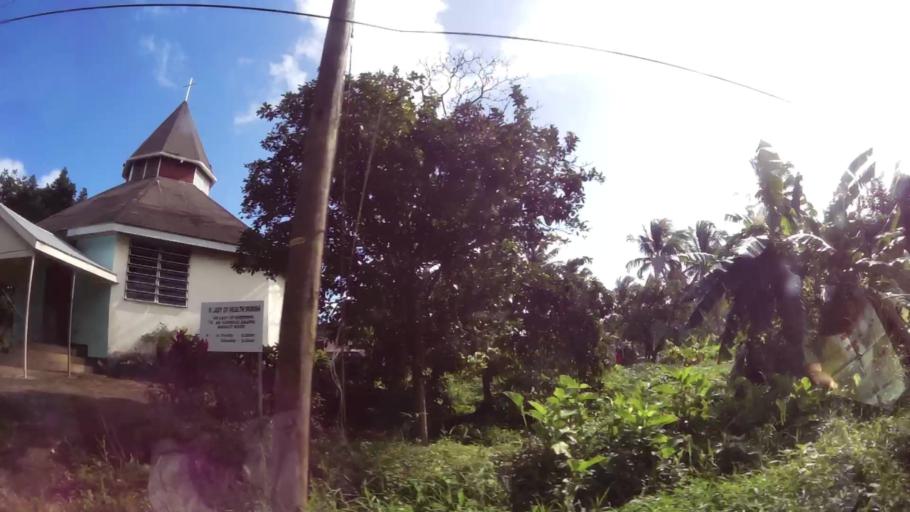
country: DM
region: Saint David
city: Castle Bruce
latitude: 15.4750
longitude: -61.2507
